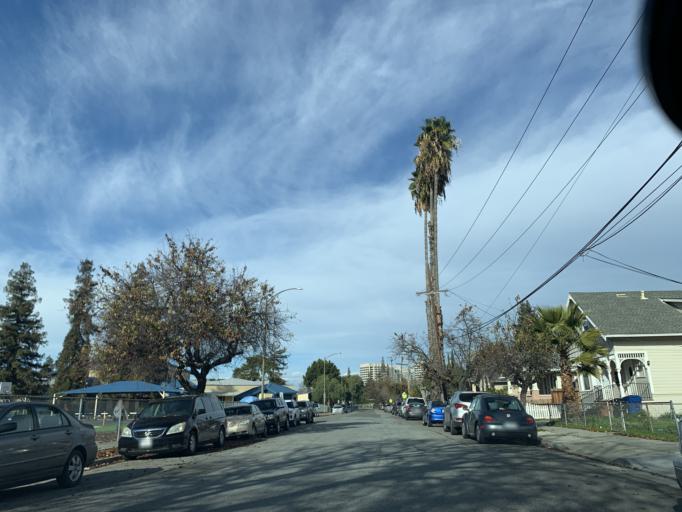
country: US
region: California
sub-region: Santa Clara County
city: San Jose
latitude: 37.3203
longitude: -121.8952
